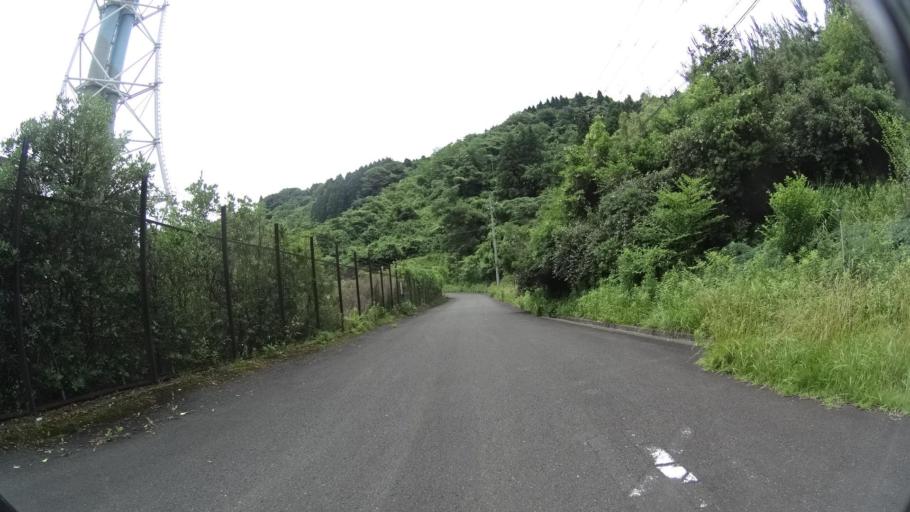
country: JP
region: Kyoto
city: Maizuru
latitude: 35.5330
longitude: 135.3465
